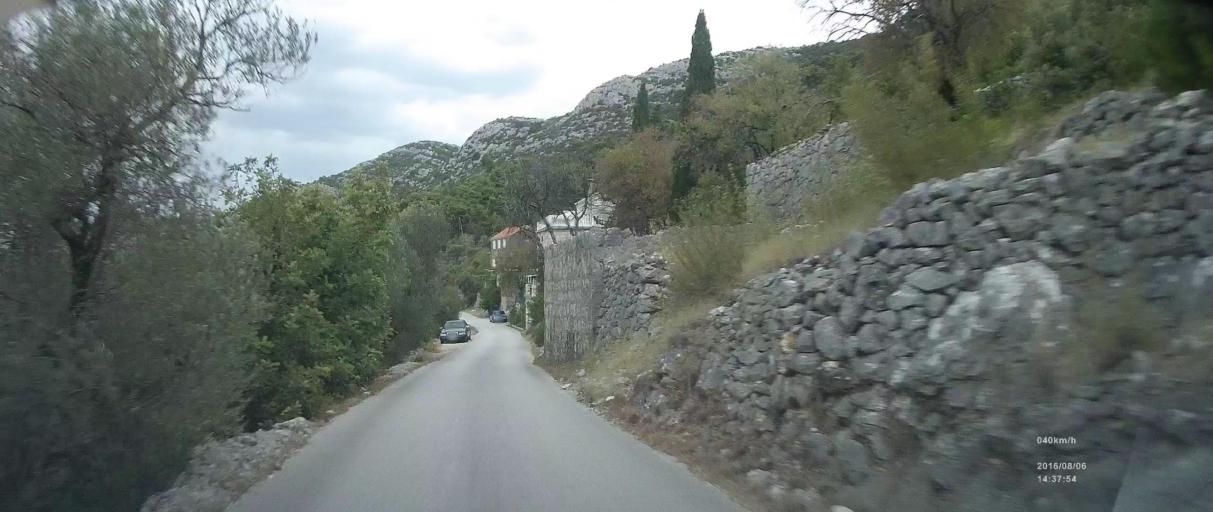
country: HR
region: Dubrovacko-Neretvanska
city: Ston
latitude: 42.7135
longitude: 17.6702
